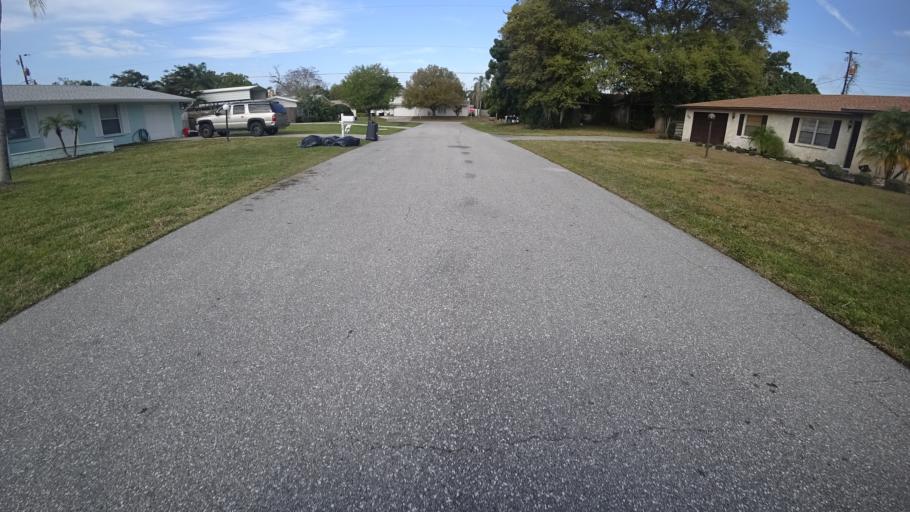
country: US
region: Florida
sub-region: Manatee County
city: Whitfield
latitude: 27.4212
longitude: -82.5536
